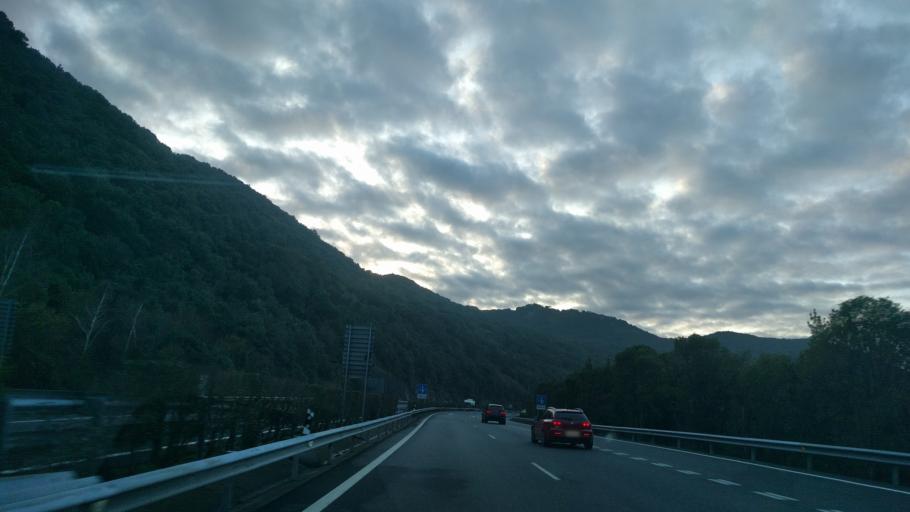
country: ES
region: Cantabria
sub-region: Provincia de Cantabria
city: Liendo
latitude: 43.3903
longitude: -3.3407
